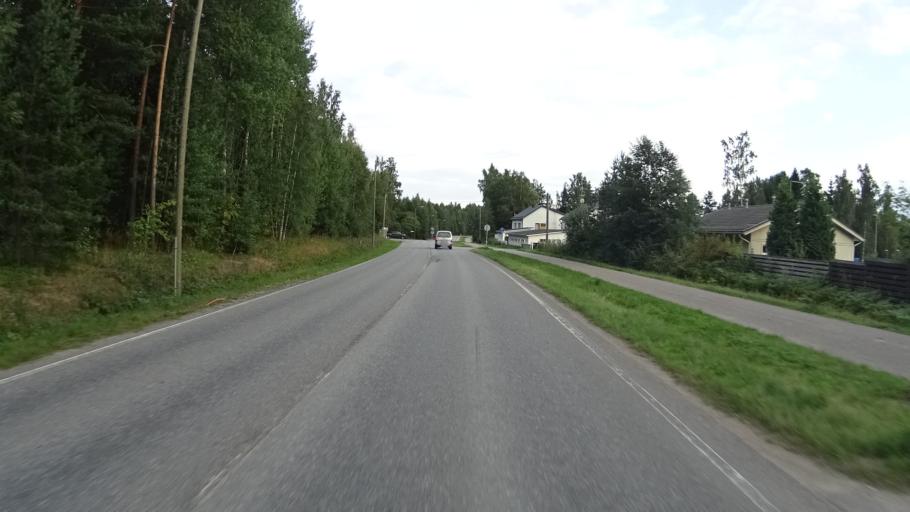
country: FI
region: Uusimaa
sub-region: Helsinki
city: Kilo
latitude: 60.3269
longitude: 24.8660
